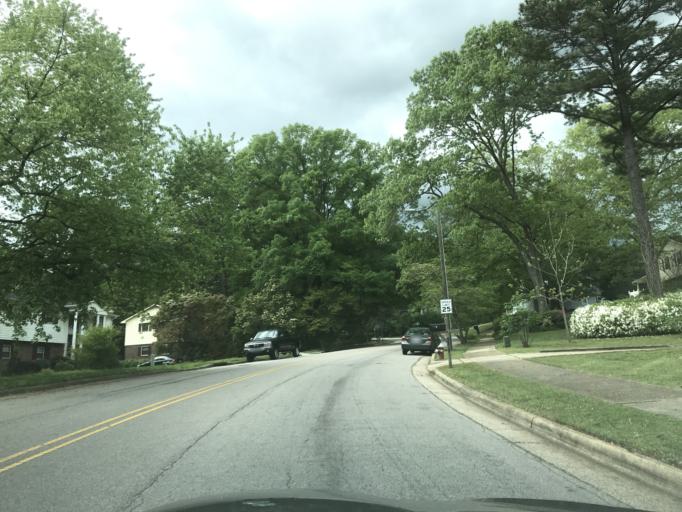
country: US
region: North Carolina
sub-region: Wake County
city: West Raleigh
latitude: 35.7733
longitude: -78.7122
